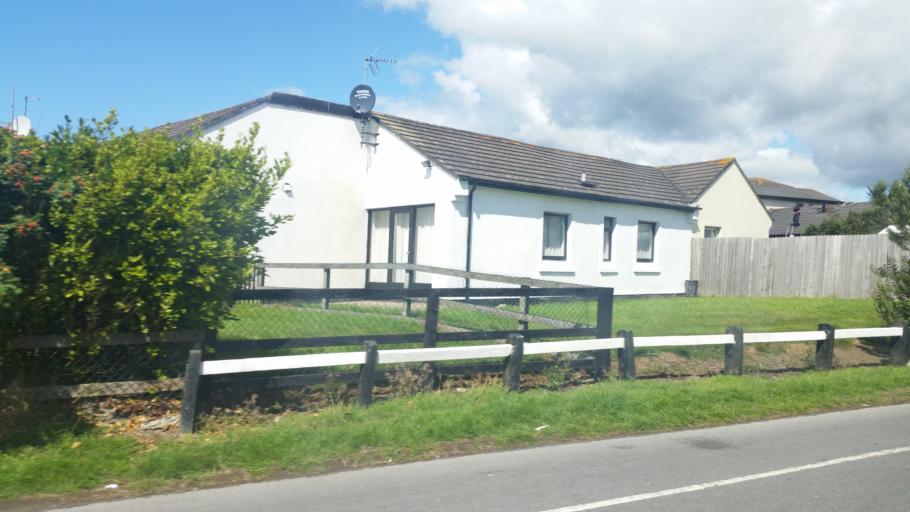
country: IE
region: Munster
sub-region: Waterford
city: Tra Mhor
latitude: 52.1636
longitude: -7.1397
